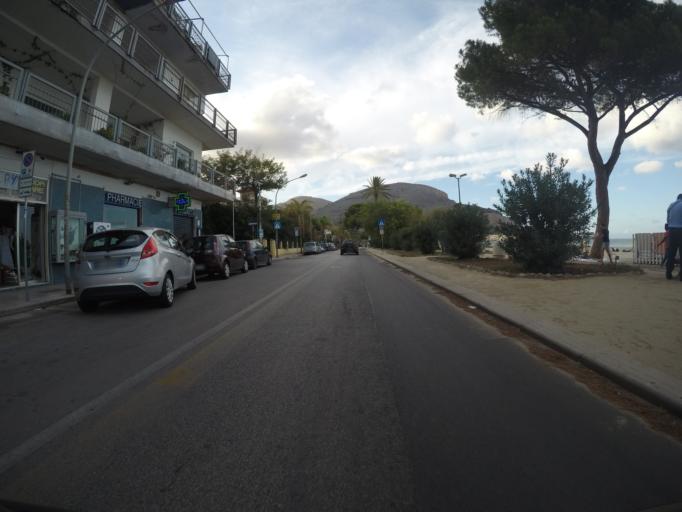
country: IT
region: Sicily
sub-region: Palermo
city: Palermo
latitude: 38.1980
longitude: 13.3304
